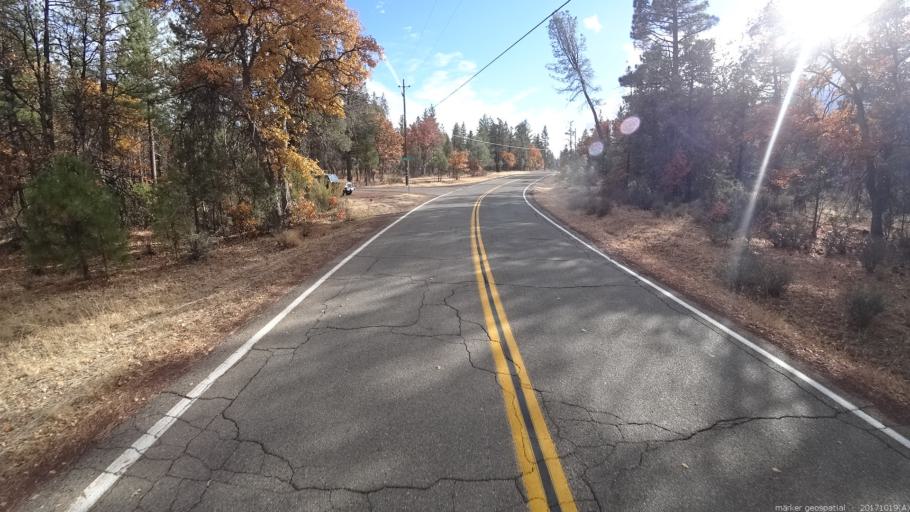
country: US
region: California
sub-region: Shasta County
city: Burney
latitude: 40.9582
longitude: -121.4393
